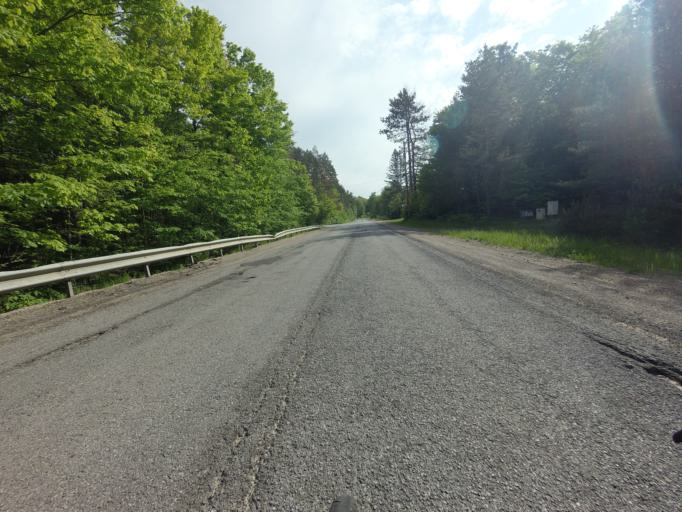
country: US
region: New York
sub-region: St. Lawrence County
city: Gouverneur
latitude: 44.2643
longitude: -75.2092
